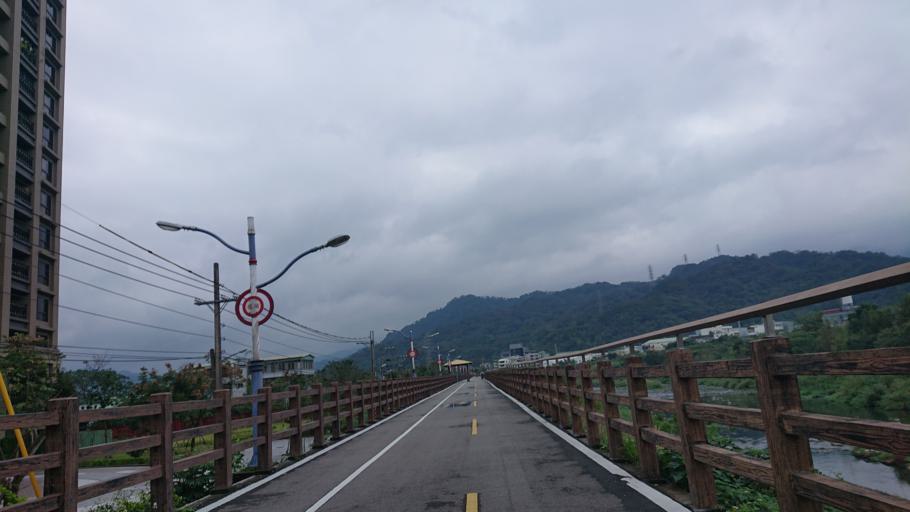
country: TW
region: Taiwan
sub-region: Taoyuan
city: Taoyuan
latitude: 24.9344
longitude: 121.3786
